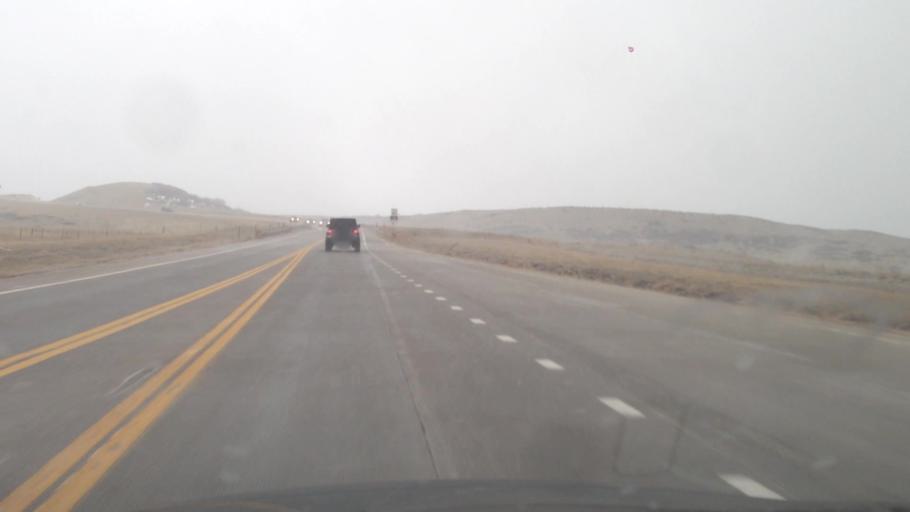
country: US
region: Colorado
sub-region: Douglas County
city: Stonegate
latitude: 39.5006
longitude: -104.8266
